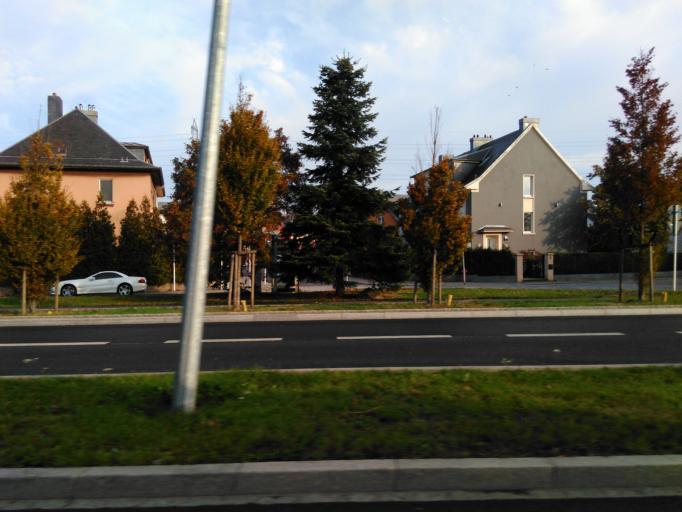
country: LU
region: Luxembourg
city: Soleuvre
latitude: 49.5090
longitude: 5.9543
